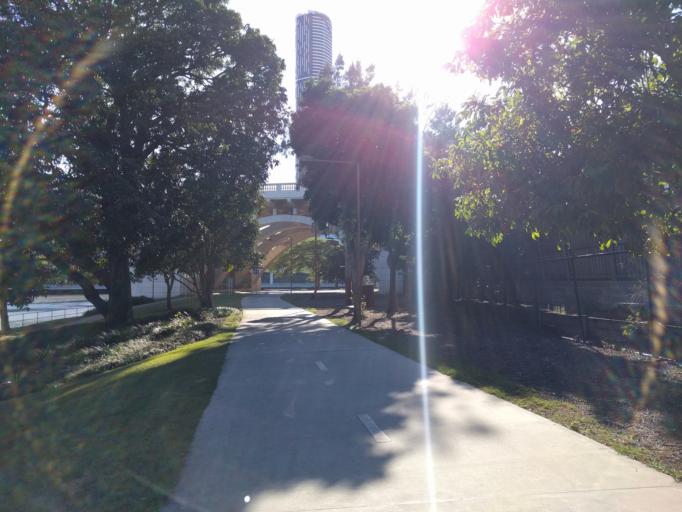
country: AU
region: Queensland
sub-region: Brisbane
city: Spring Hill
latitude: -27.4699
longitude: 153.0151
